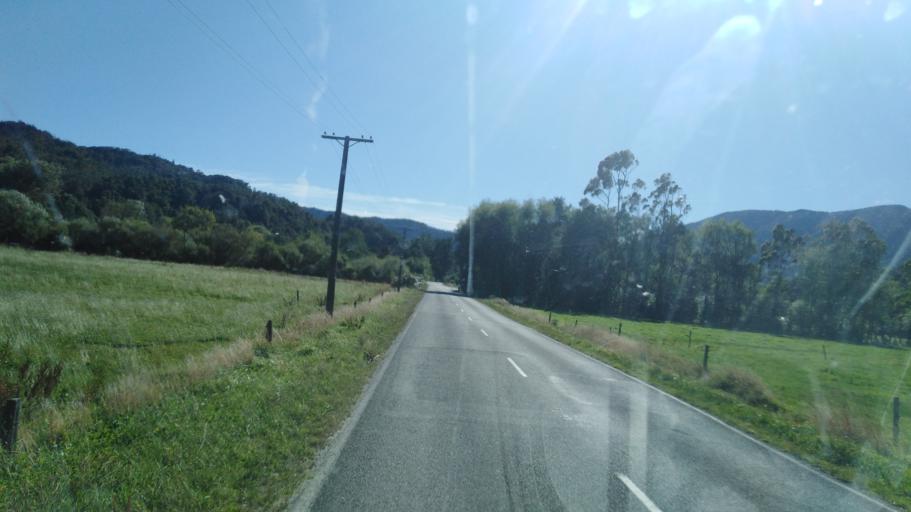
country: NZ
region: West Coast
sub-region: Buller District
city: Westport
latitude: -41.5313
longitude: 171.9640
